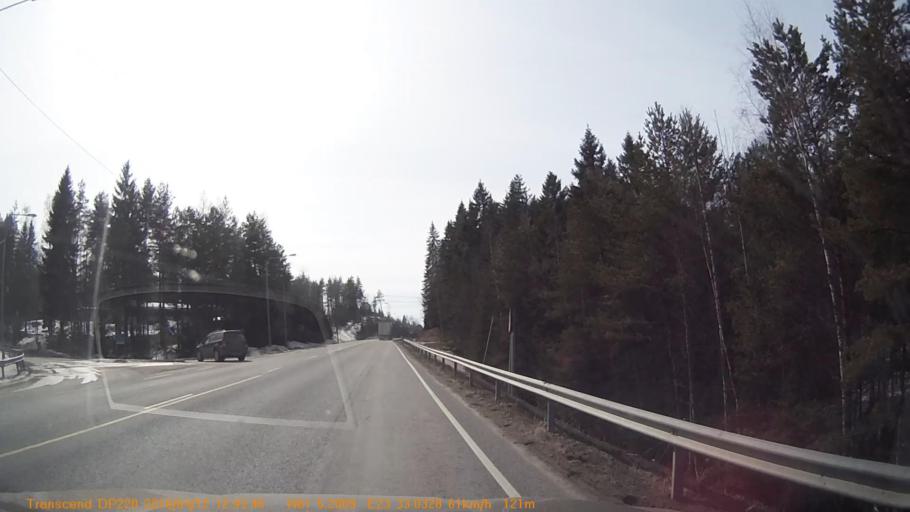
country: FI
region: Pirkanmaa
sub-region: Etelae-Pirkanmaa
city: Urjala
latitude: 61.0866
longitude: 23.5504
